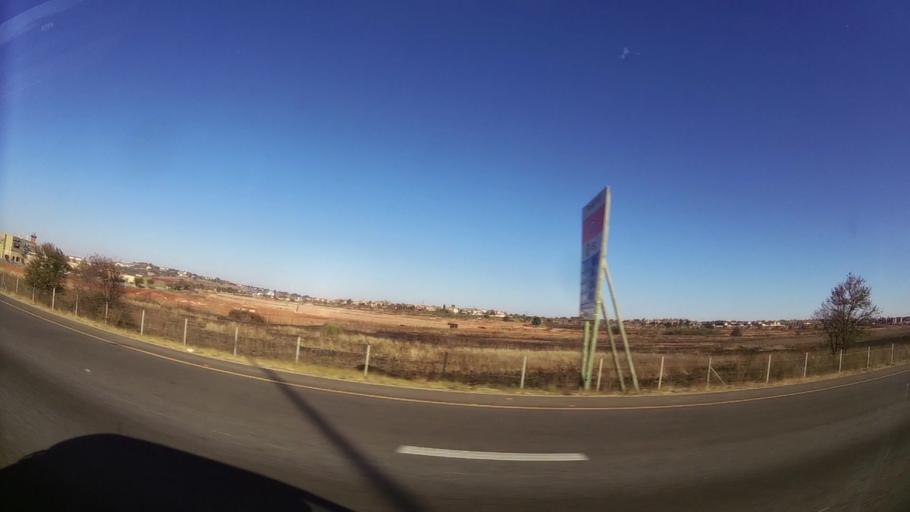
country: ZA
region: Gauteng
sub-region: City of Tshwane Metropolitan Municipality
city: Centurion
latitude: -25.8577
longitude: 28.2525
